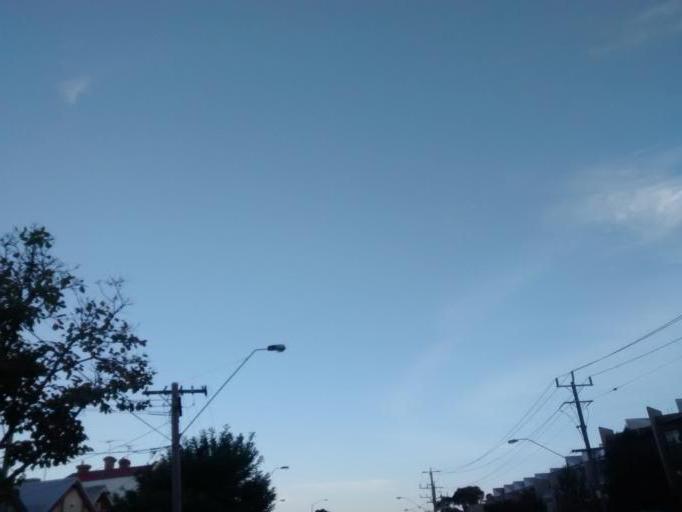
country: AU
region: Victoria
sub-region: Port Phillip
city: Port Melbourne
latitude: -37.8347
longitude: 144.9479
